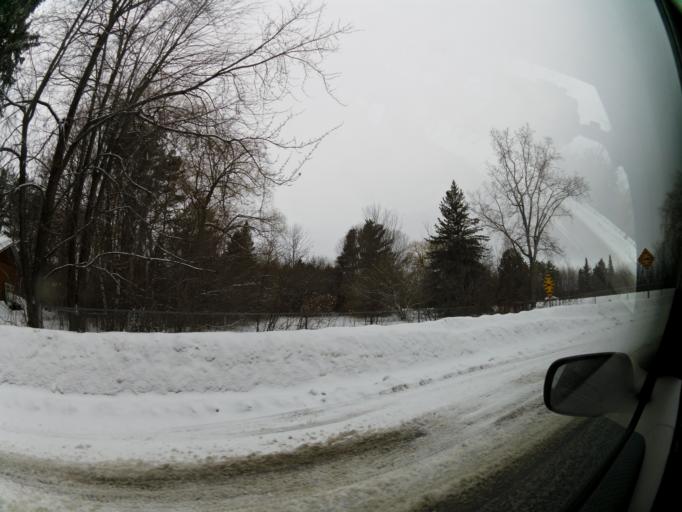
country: CA
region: Quebec
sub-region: Outaouais
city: Gatineau
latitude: 45.4620
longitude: -75.6145
